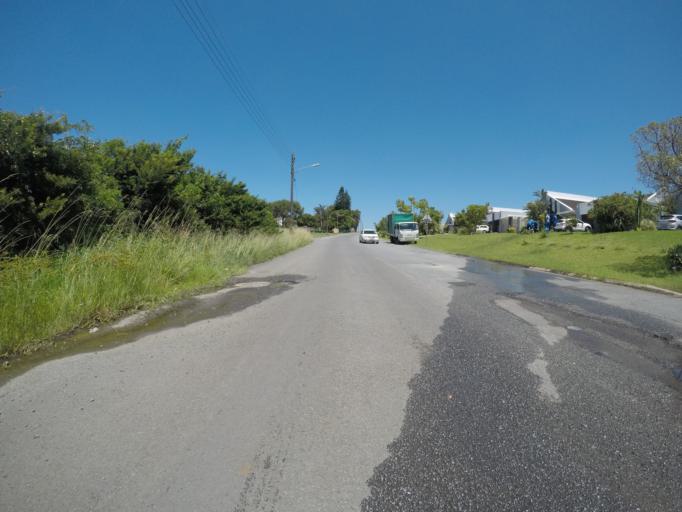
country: ZA
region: Eastern Cape
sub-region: Buffalo City Metropolitan Municipality
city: East London
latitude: -32.9639
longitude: 27.9542
